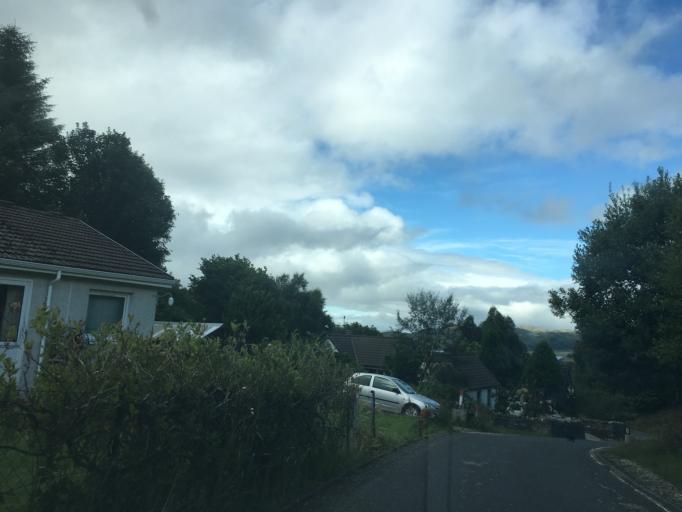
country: GB
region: Scotland
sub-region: Argyll and Bute
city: Ardrishaig
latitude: 56.0890
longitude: -5.5605
